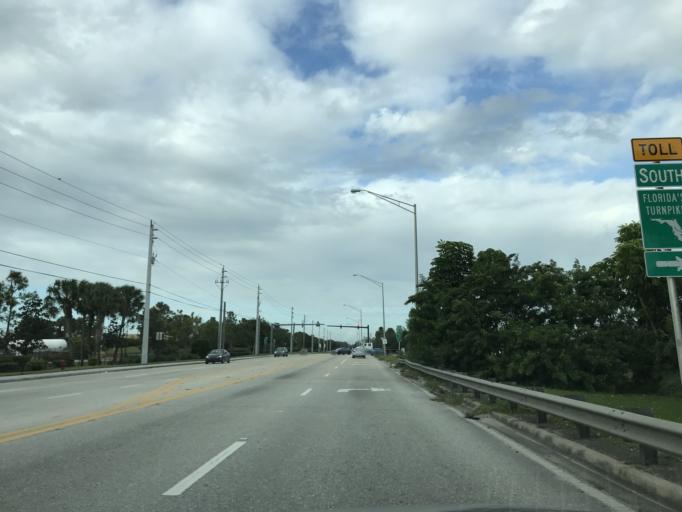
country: US
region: Florida
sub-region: Palm Beach County
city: Lake Belvedere Estates
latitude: 26.6841
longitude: -80.1658
